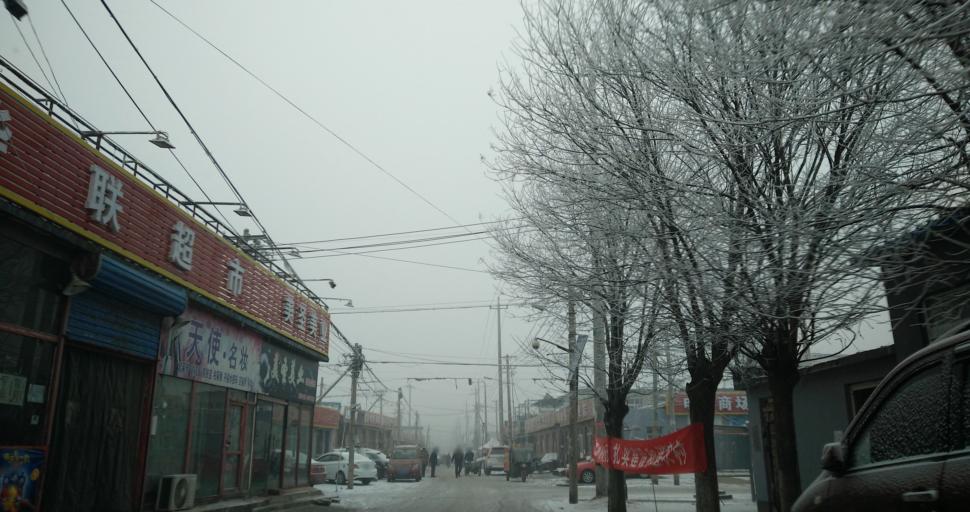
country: CN
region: Beijing
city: Yinghai
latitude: 39.7169
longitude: 116.4273
